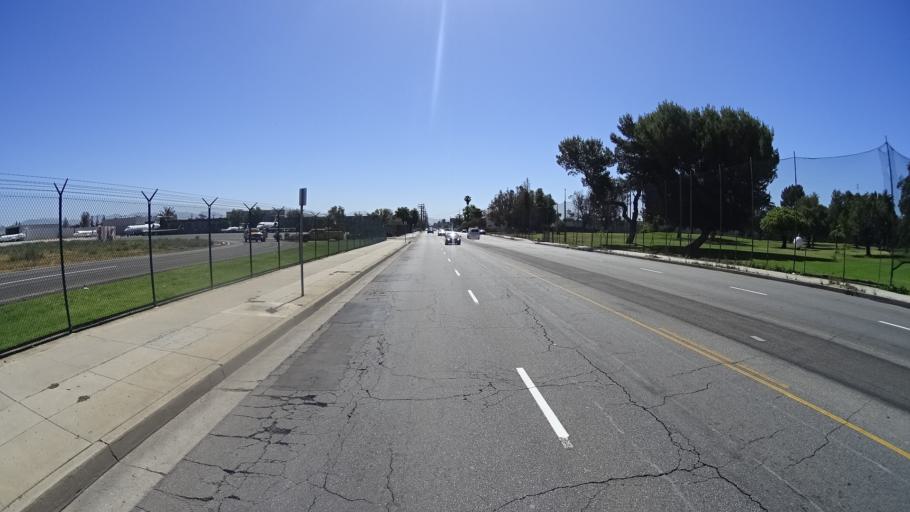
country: US
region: California
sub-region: Los Angeles County
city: Van Nuys
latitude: 34.1941
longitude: -118.4889
